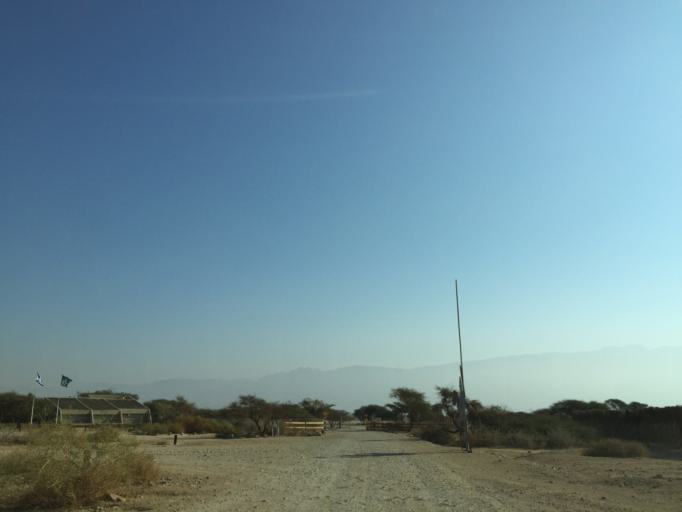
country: JO
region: Ma'an
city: Al Quwayrah
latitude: 29.8456
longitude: 35.0288
